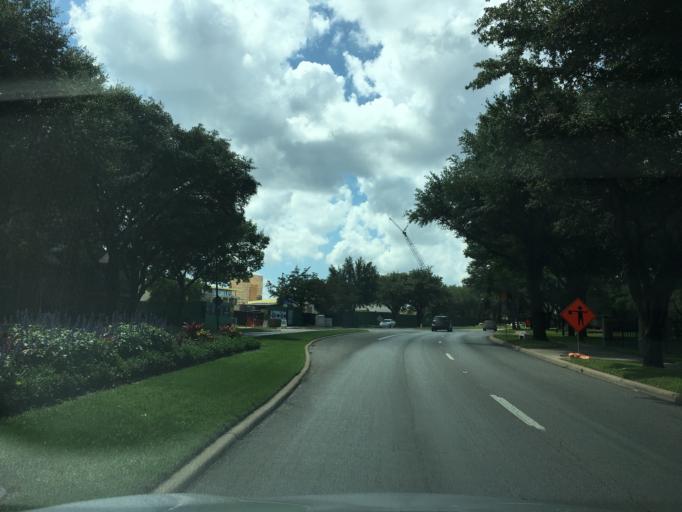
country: US
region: Texas
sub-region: Dallas County
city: Highland Park
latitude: 32.8590
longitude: -96.7599
